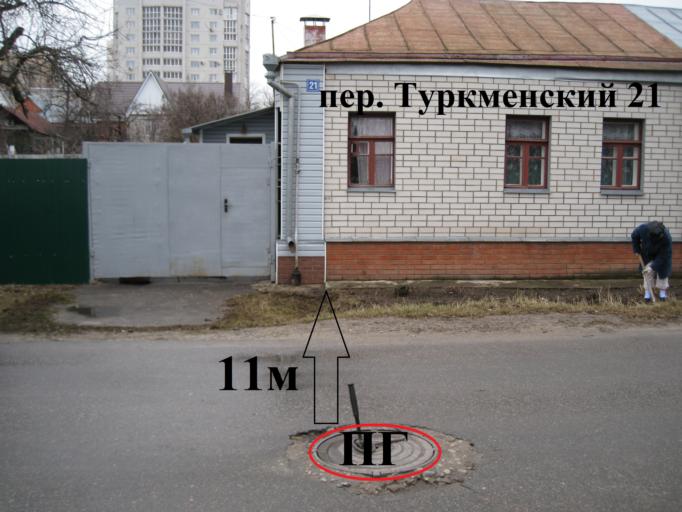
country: RU
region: Voronezj
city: Voronezh
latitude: 51.6385
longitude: 39.1720
